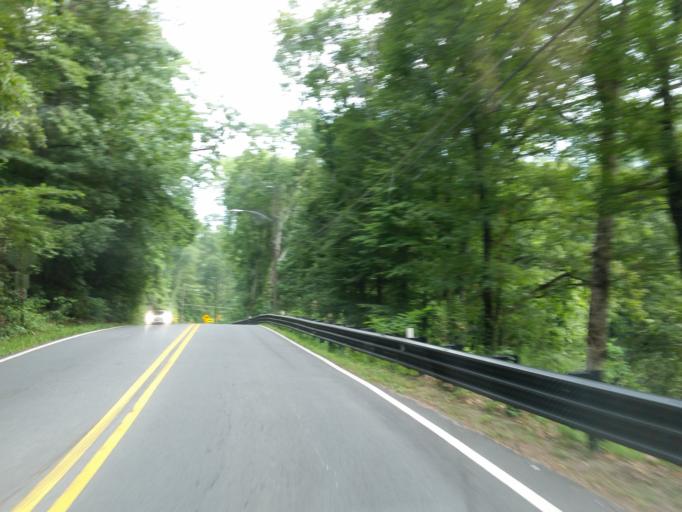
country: US
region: Georgia
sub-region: Fulton County
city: Sandy Springs
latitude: 33.9424
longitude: -84.4379
